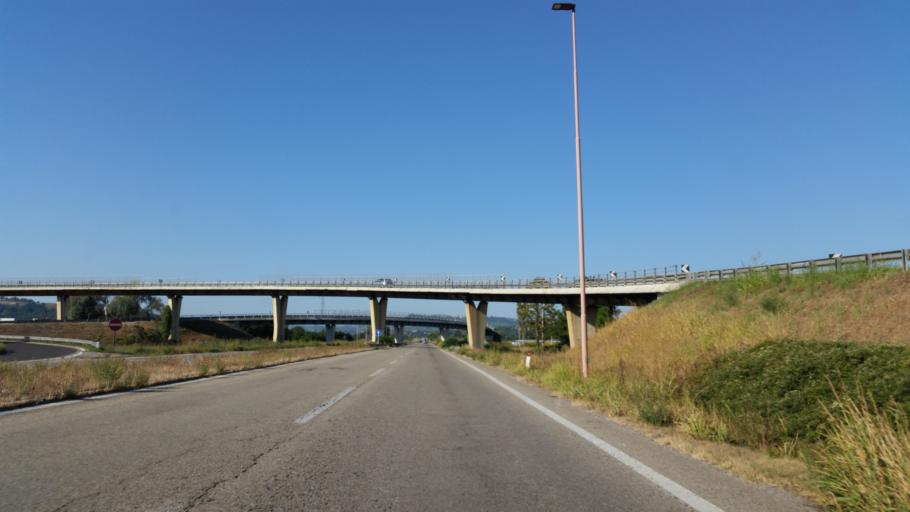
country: IT
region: Piedmont
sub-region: Provincia di Cuneo
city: Alba
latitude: 44.6994
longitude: 8.0101
